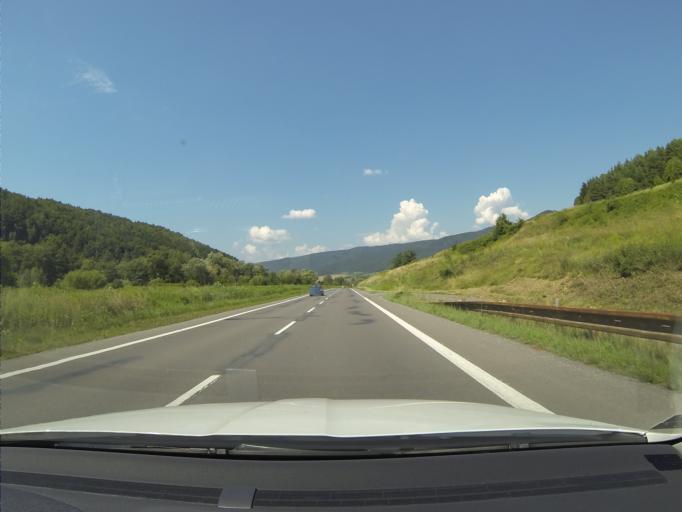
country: SK
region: Nitriansky
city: Handlova
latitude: 48.7507
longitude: 18.7635
